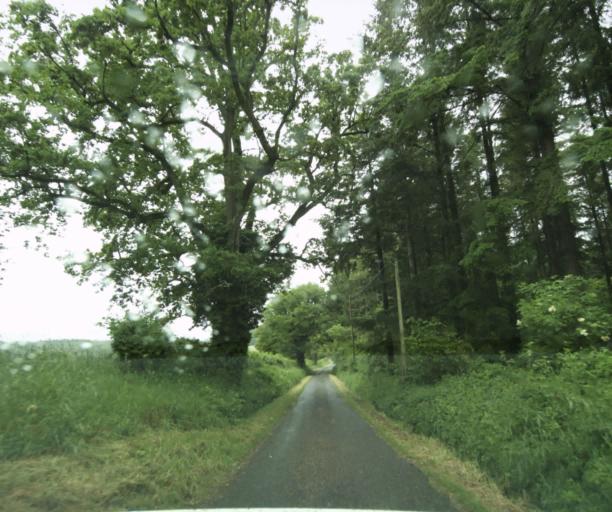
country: FR
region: Bourgogne
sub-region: Departement de Saone-et-Loire
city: Saint-Vallier
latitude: 46.4946
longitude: 4.4631
